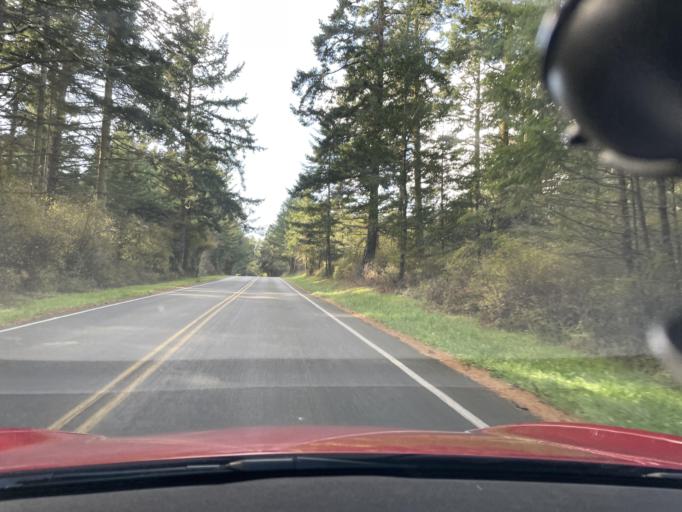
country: US
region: Washington
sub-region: San Juan County
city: Friday Harbor
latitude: 48.4692
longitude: -123.0170
